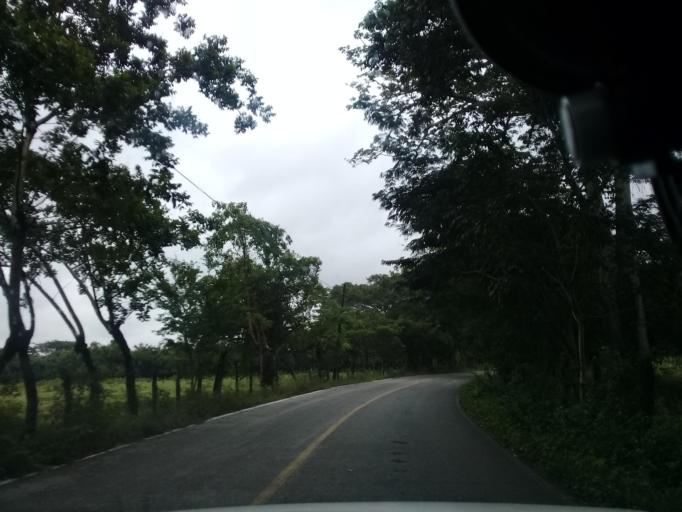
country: MX
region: Veracruz
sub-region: Chalma
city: San Pedro Coyutla
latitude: 21.2099
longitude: -98.4107
